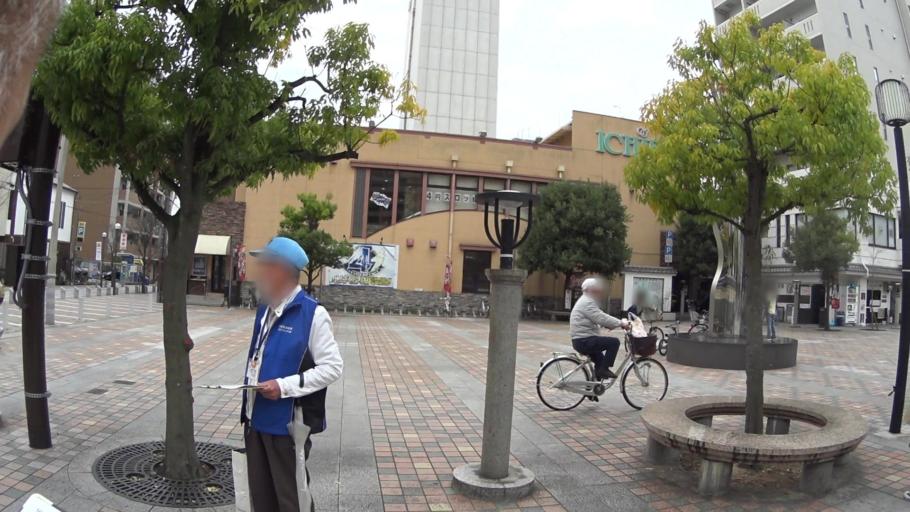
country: JP
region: Hyogo
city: Itami
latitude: 34.7815
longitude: 135.4170
